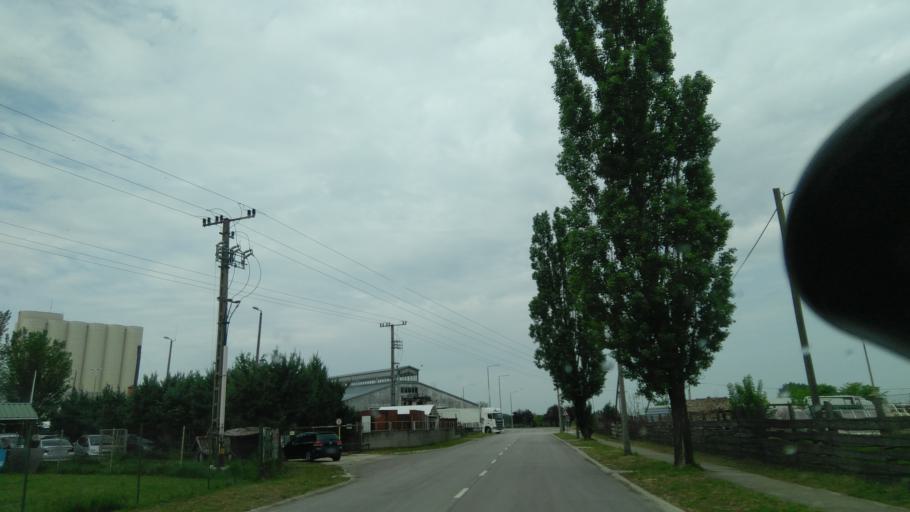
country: HU
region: Bekes
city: Szeghalom
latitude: 47.0174
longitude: 21.1520
